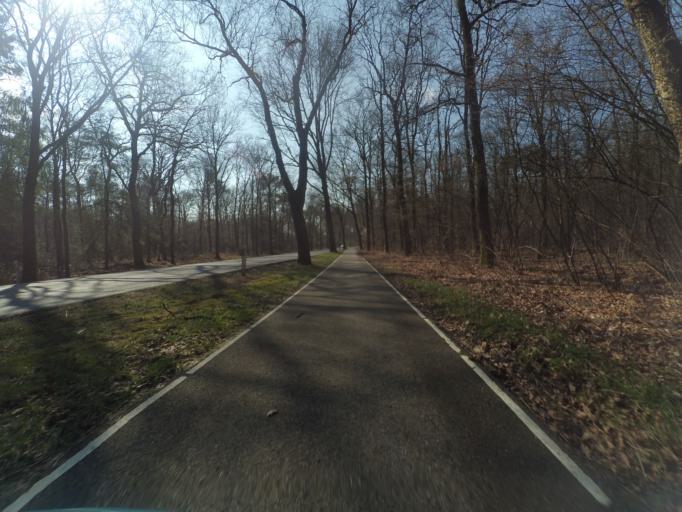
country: NL
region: Gelderland
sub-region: Gemeente Apeldoorn
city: Beekbergen
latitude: 52.1299
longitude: 5.8798
